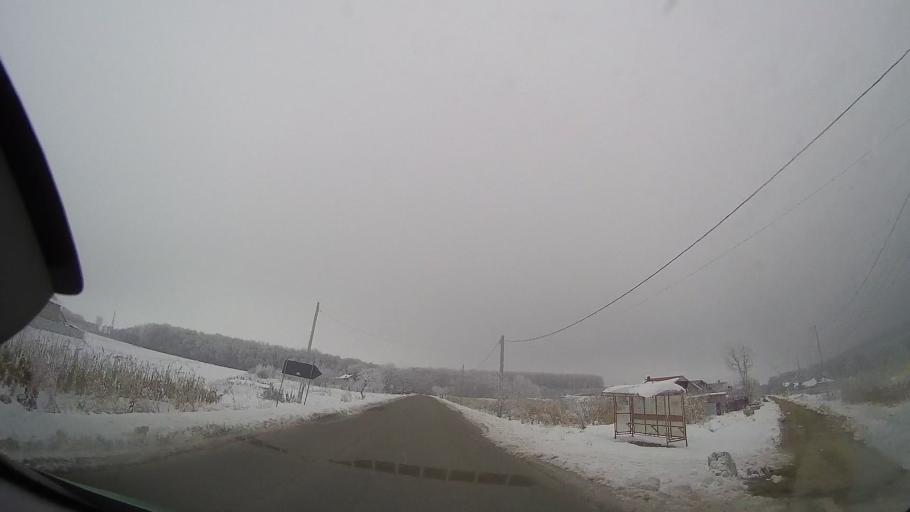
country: RO
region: Neamt
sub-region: Comuna Horia
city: Cotu Vames
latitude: 46.8779
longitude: 26.9752
